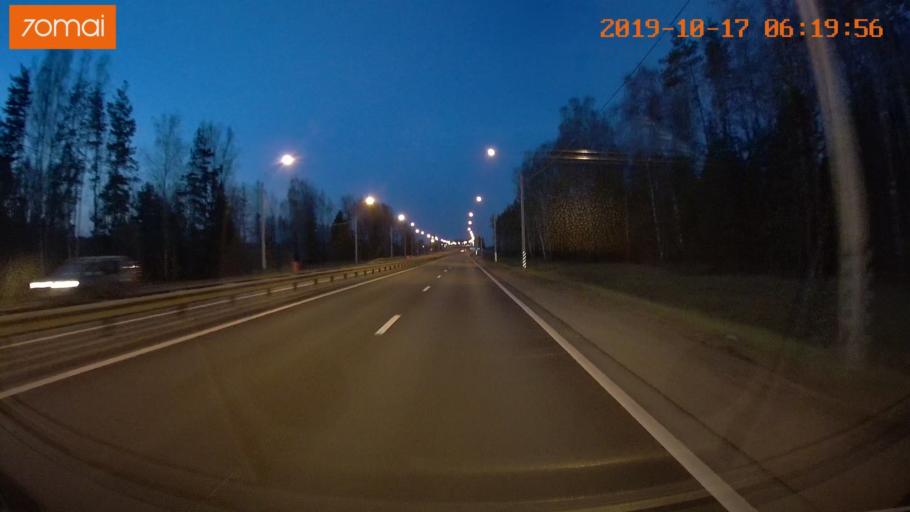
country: RU
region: Ivanovo
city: Lezhnevo
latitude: 56.8222
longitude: 40.8939
